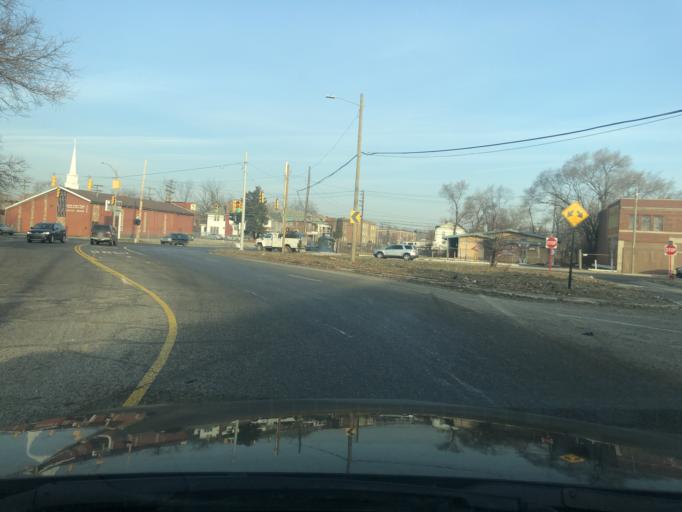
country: US
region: Michigan
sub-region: Wayne County
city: Highland Park
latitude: 42.4025
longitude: -83.1268
